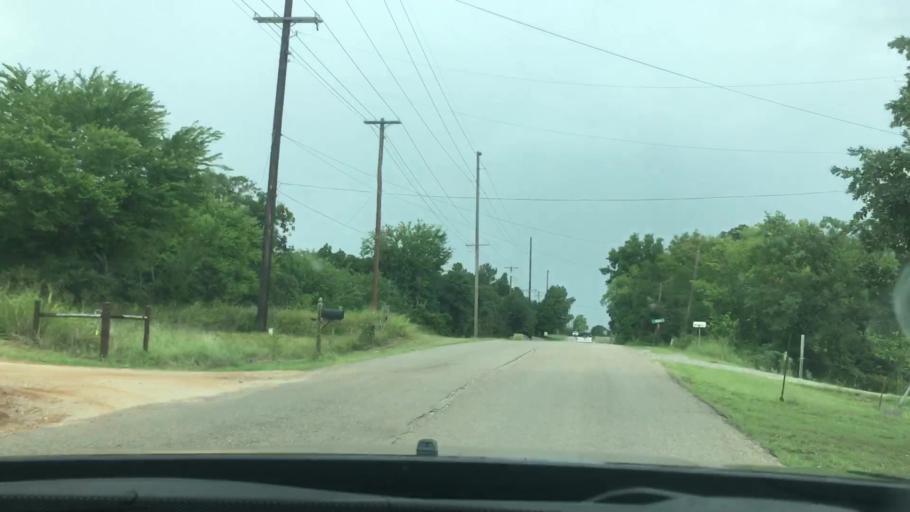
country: US
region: Oklahoma
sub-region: Carter County
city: Healdton
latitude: 34.2198
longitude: -97.4922
